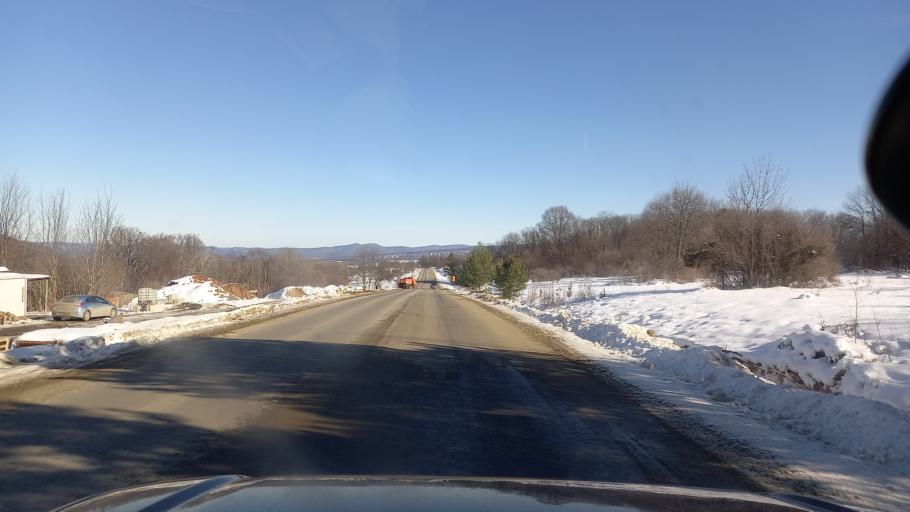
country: RU
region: Adygeya
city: Kamennomostskiy
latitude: 44.2226
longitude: 40.0996
